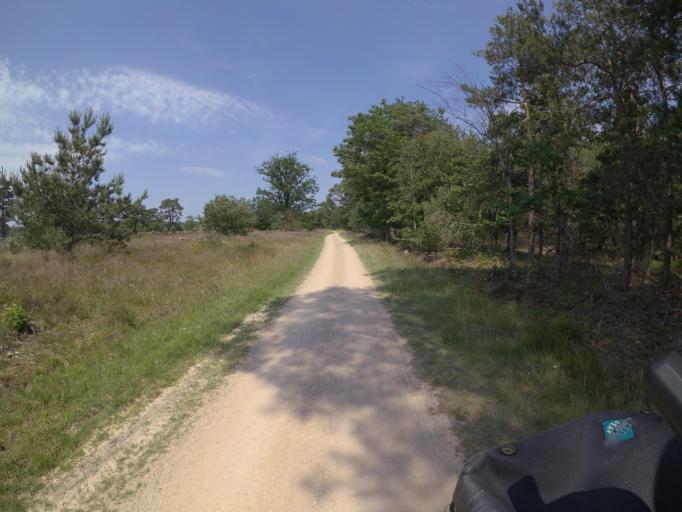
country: NL
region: Overijssel
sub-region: Gemeente Hof van Twente
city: Markelo
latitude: 52.3472
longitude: 6.4478
